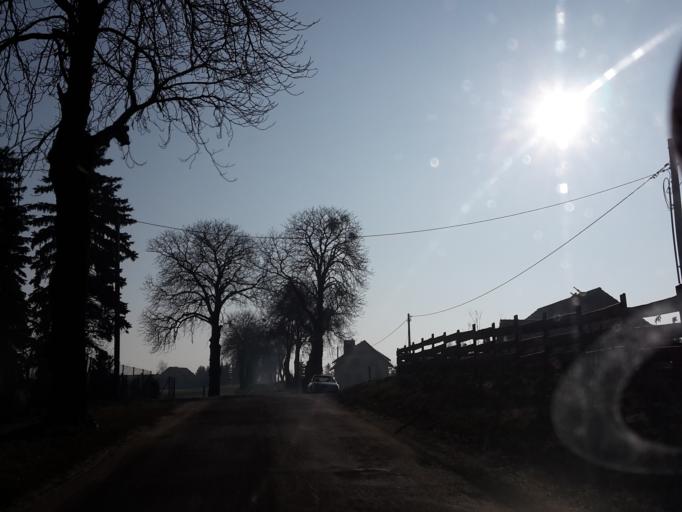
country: PL
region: Kujawsko-Pomorskie
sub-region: Powiat brodnicki
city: Brodnica
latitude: 53.2959
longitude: 19.4026
